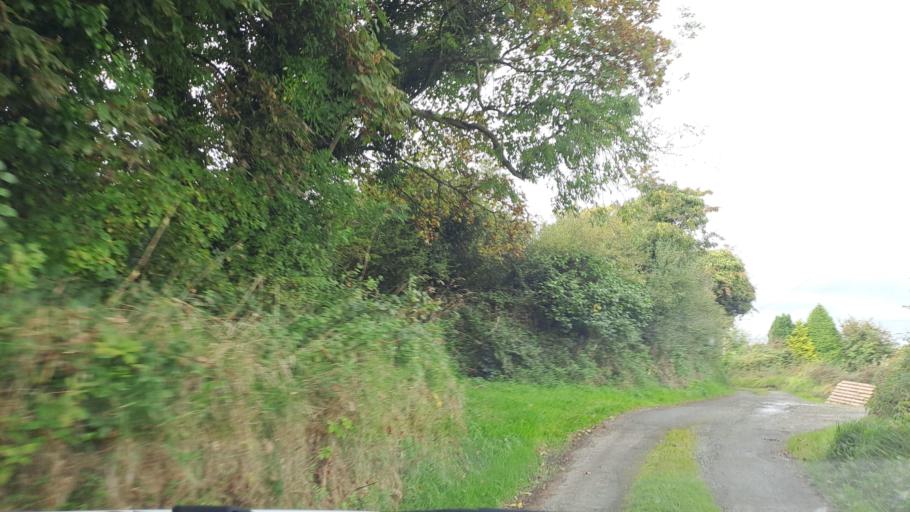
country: IE
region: Ulster
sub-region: An Cabhan
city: Bailieborough
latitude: 54.0003
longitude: -6.9398
